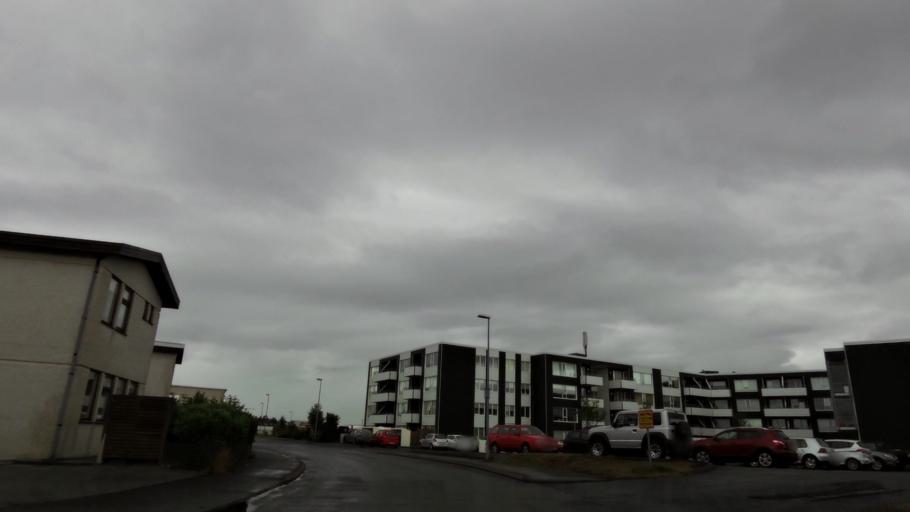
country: IS
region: Capital Region
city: Hafnarfjoerdur
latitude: 64.0489
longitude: -21.9761
